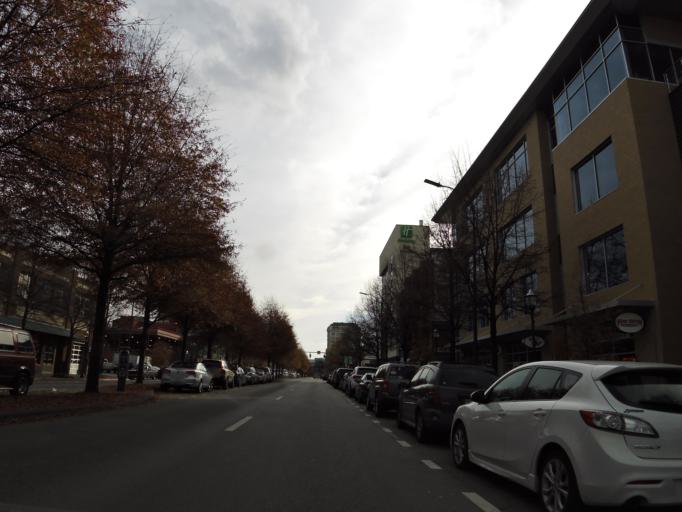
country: US
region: Tennessee
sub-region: Hamilton County
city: Chattanooga
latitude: 35.0520
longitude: -85.3108
